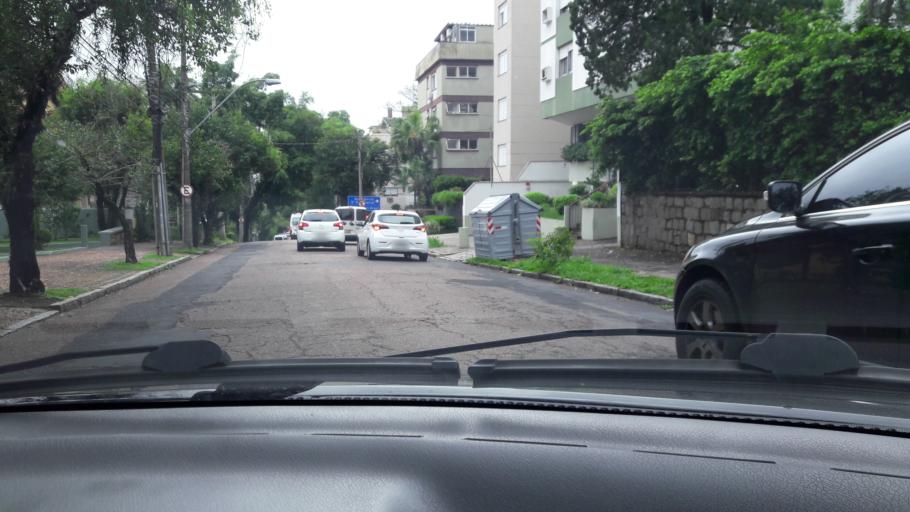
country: BR
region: Rio Grande do Sul
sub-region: Porto Alegre
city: Porto Alegre
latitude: -30.0282
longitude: -51.1961
